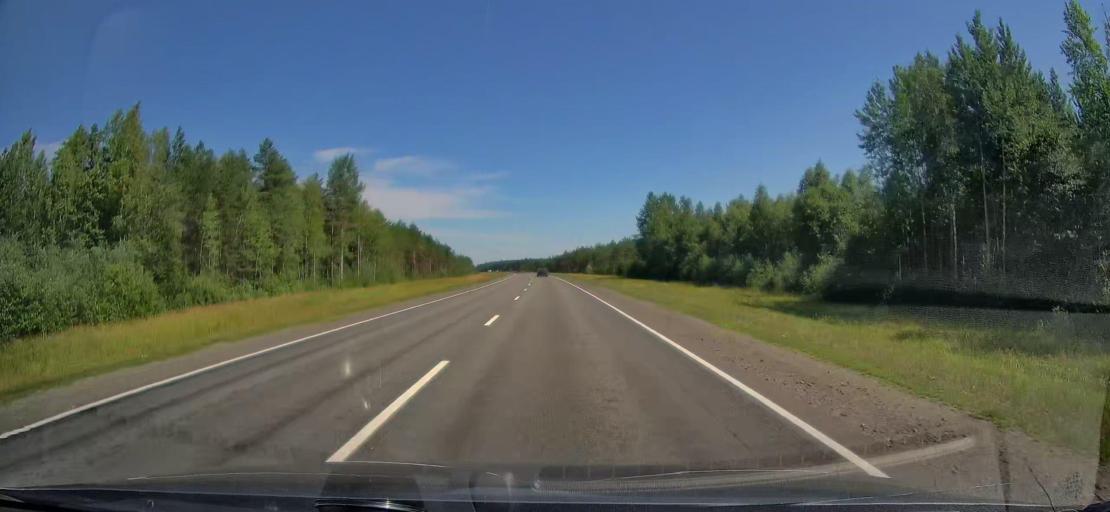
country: RU
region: Tverskaya
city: Ves'yegonsk
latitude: 58.9269
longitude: 37.2498
